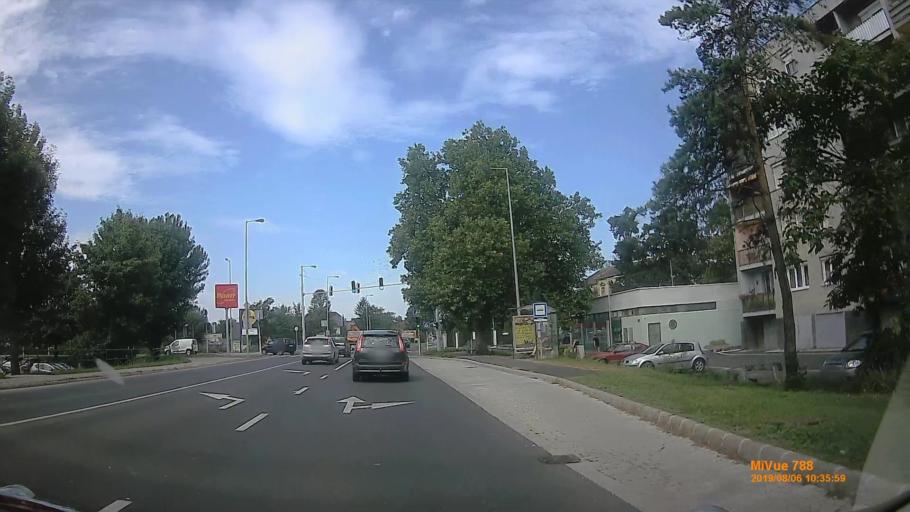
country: HU
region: Vas
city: Kormend
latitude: 47.0097
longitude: 16.5941
